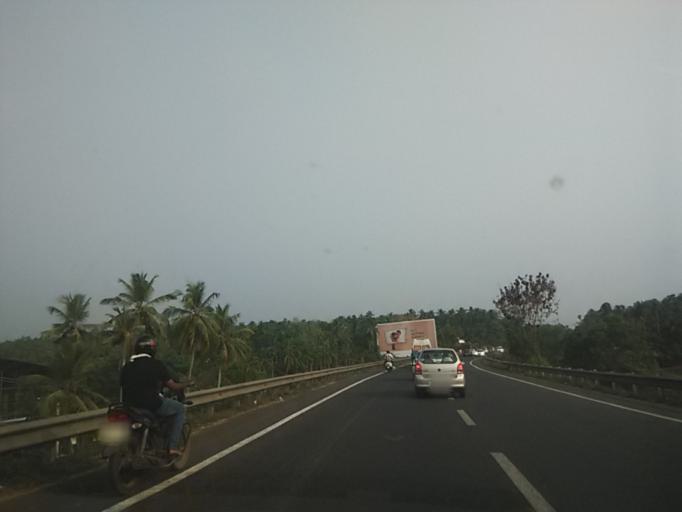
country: IN
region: Kerala
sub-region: Kozhikode
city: Kozhikode
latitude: 11.2971
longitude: 75.7960
